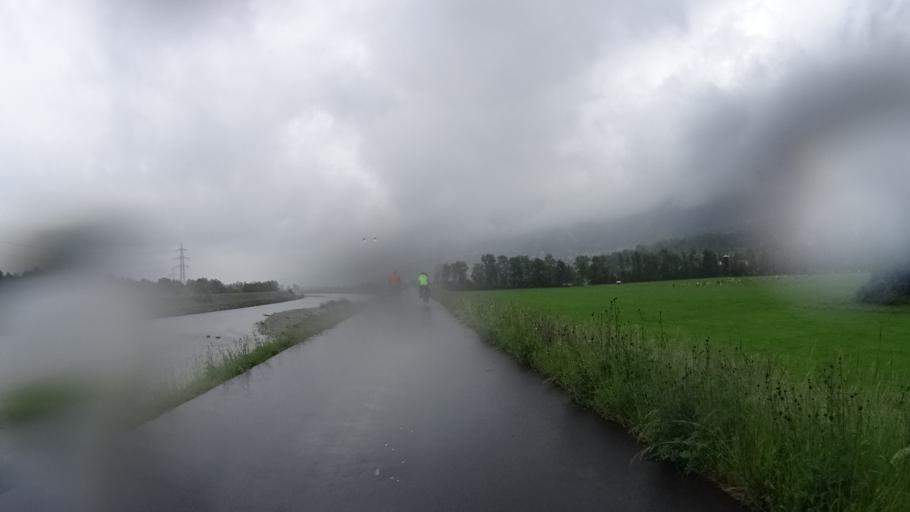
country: LI
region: Triesen
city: Triesen
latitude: 47.0905
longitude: 9.5179
